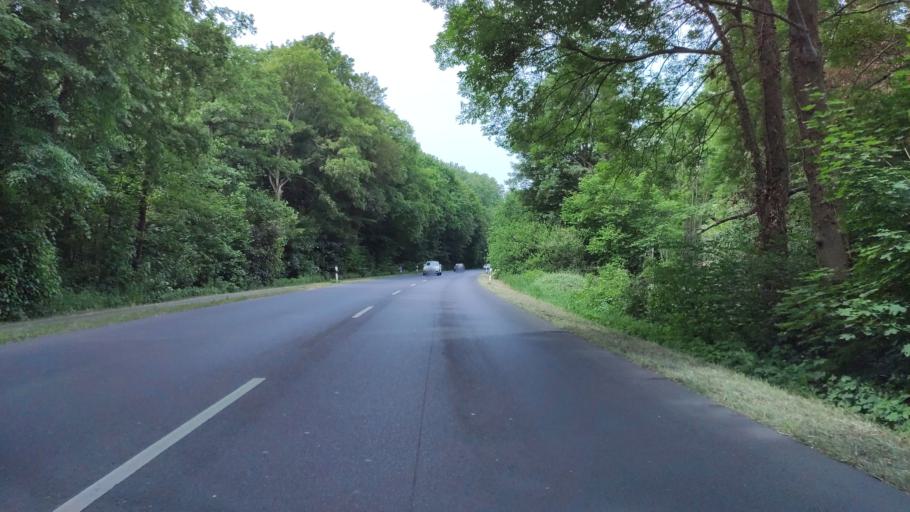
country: DE
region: North Rhine-Westphalia
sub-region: Regierungsbezirk Dusseldorf
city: Korschenbroich
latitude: 51.1941
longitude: 6.4871
